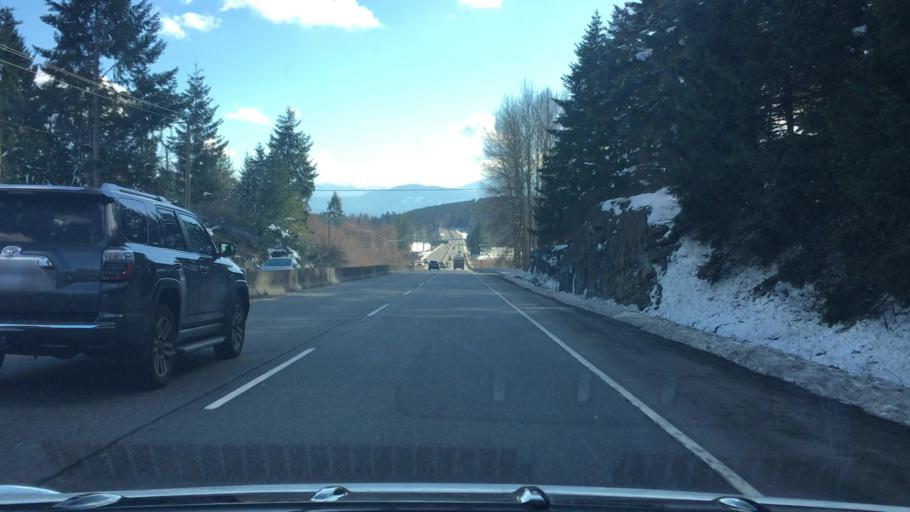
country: CA
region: British Columbia
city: Nanaimo
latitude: 49.0871
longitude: -123.8833
